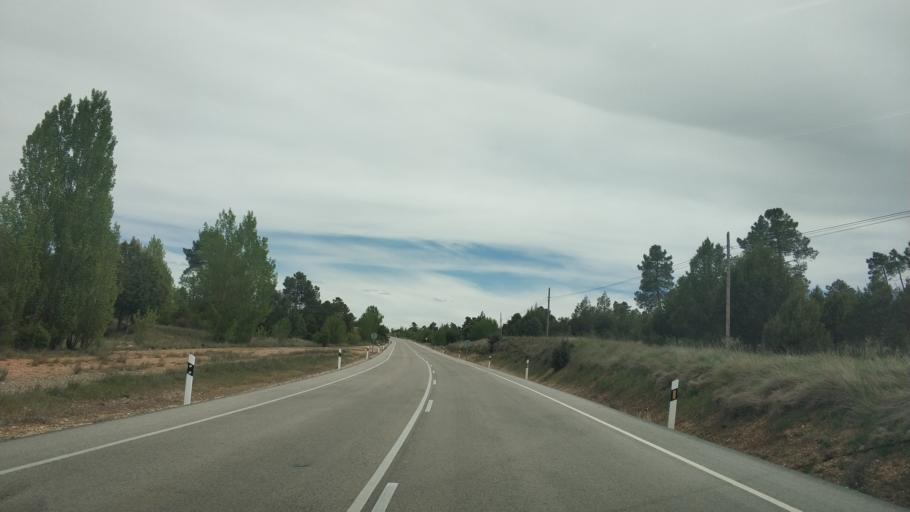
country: ES
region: Castille and Leon
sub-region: Provincia de Soria
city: Valdenebro
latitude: 41.5473
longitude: -2.9606
